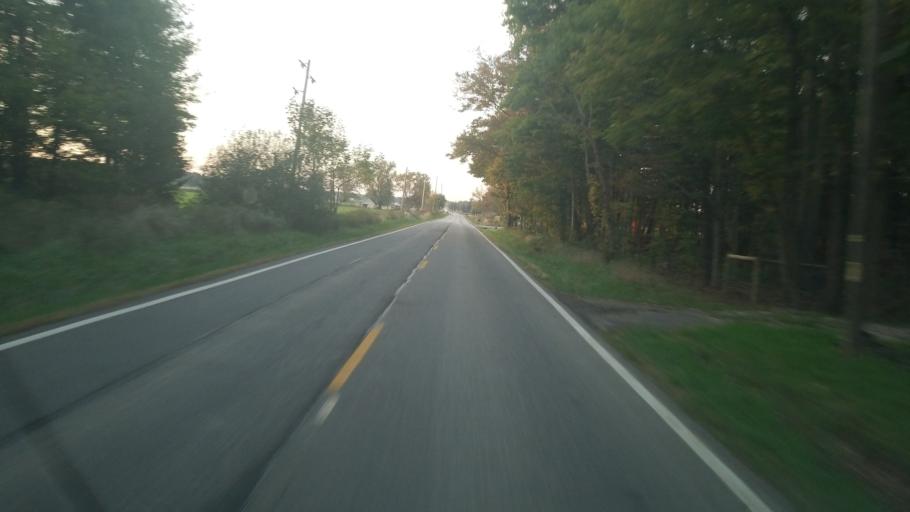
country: US
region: Ohio
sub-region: Ashtabula County
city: Andover
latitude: 41.6555
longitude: -80.6670
